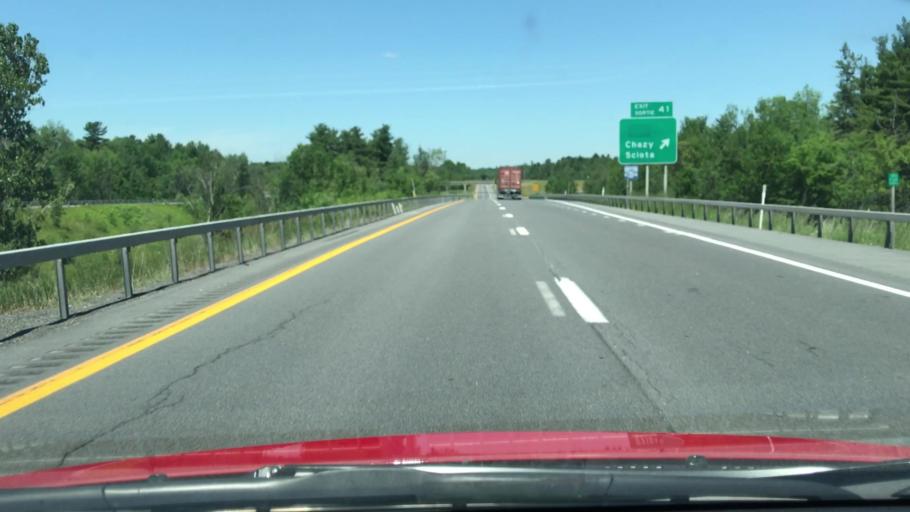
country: US
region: New York
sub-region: Clinton County
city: Champlain
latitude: 44.8851
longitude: -73.4517
